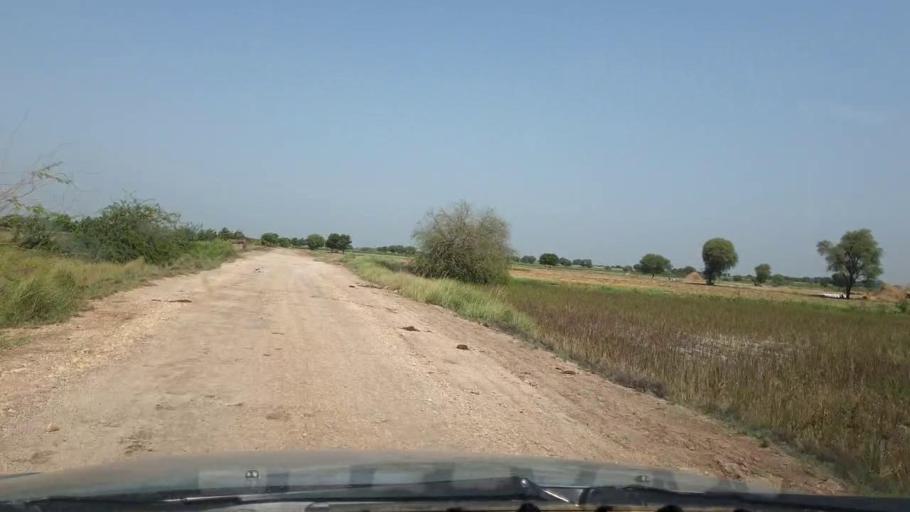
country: PK
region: Sindh
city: Tando Muhammad Khan
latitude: 25.1703
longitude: 68.6338
